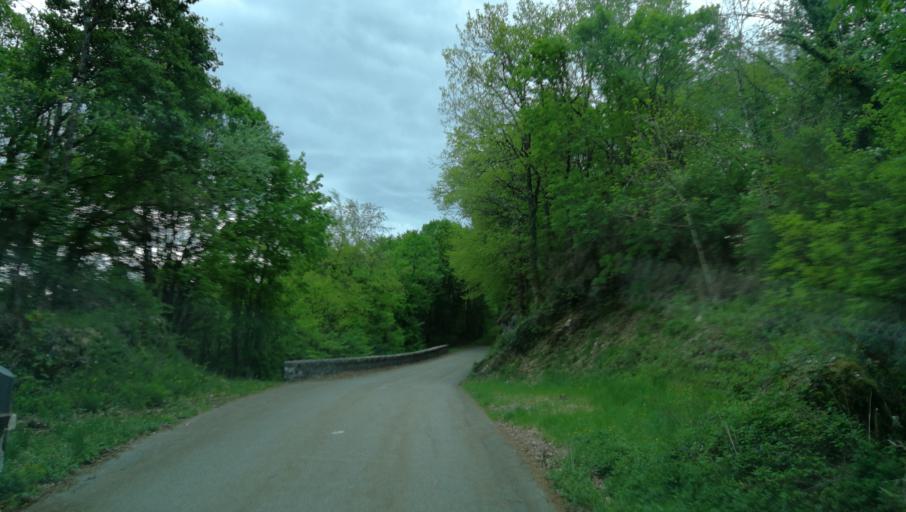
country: FR
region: Rhone-Alpes
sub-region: Departement de la Savoie
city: Chatillon
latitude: 45.7541
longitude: 5.8297
